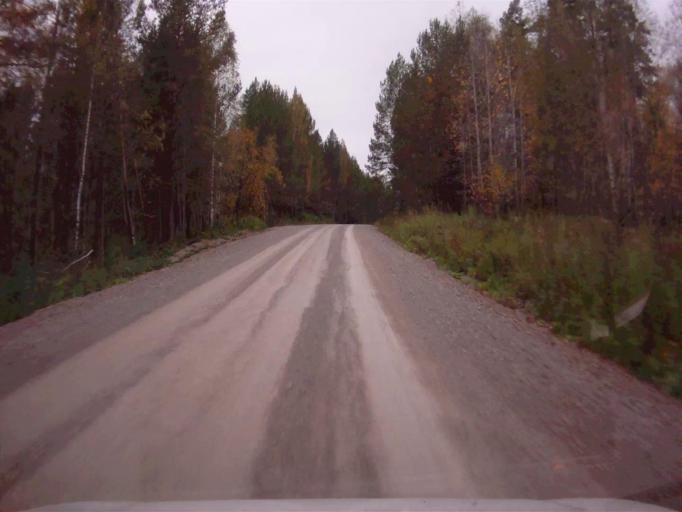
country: RU
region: Chelyabinsk
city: Nyazepetrovsk
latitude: 56.0581
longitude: 59.4562
